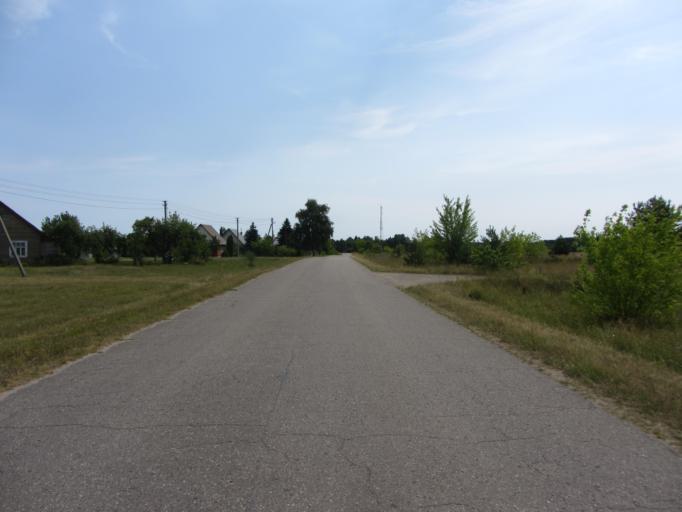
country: LT
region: Alytaus apskritis
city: Druskininkai
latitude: 54.0857
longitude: 23.9718
